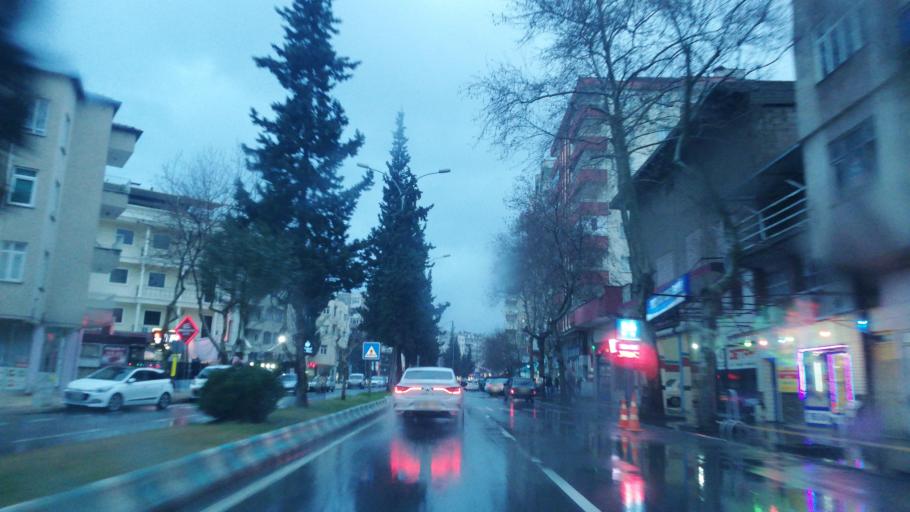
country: TR
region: Kahramanmaras
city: Kahramanmaras
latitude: 37.5731
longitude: 36.9357
